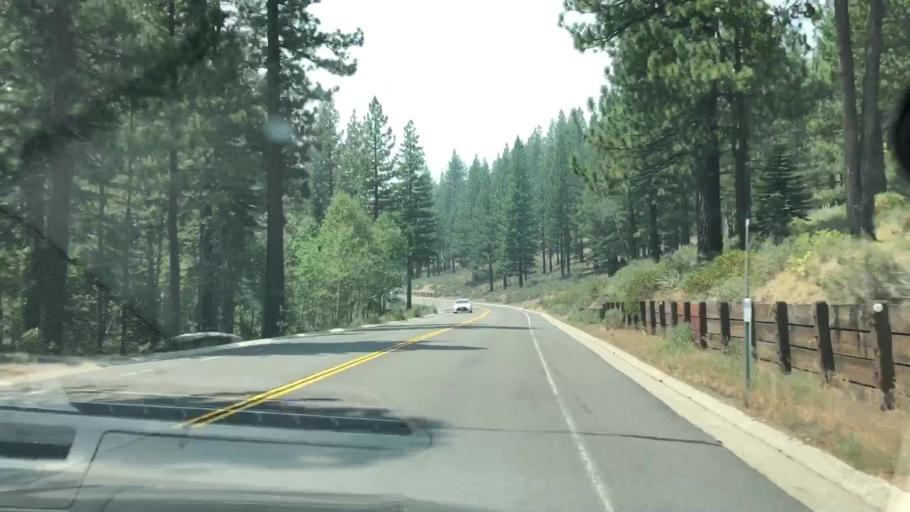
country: US
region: California
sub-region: El Dorado County
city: South Lake Tahoe
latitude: 38.8625
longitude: -120.0044
